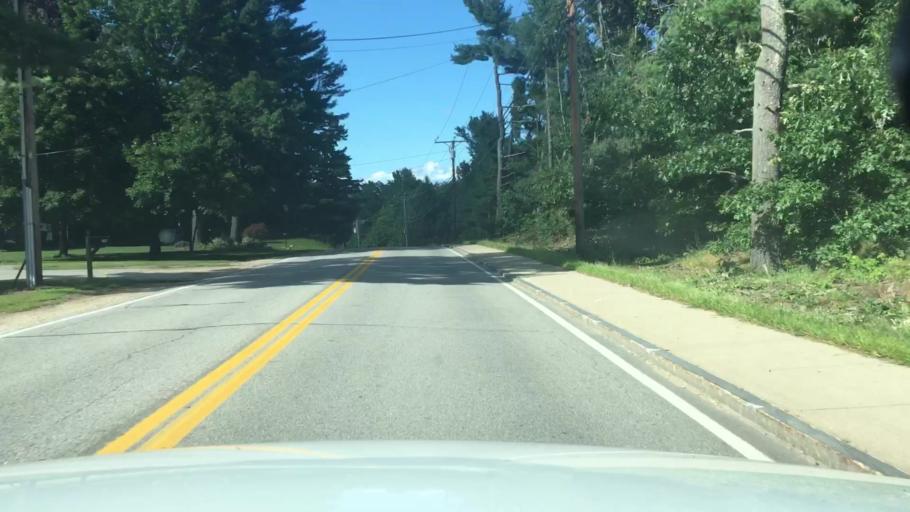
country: US
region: New Hampshire
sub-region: Strafford County
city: Dover
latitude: 43.1668
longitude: -70.8728
